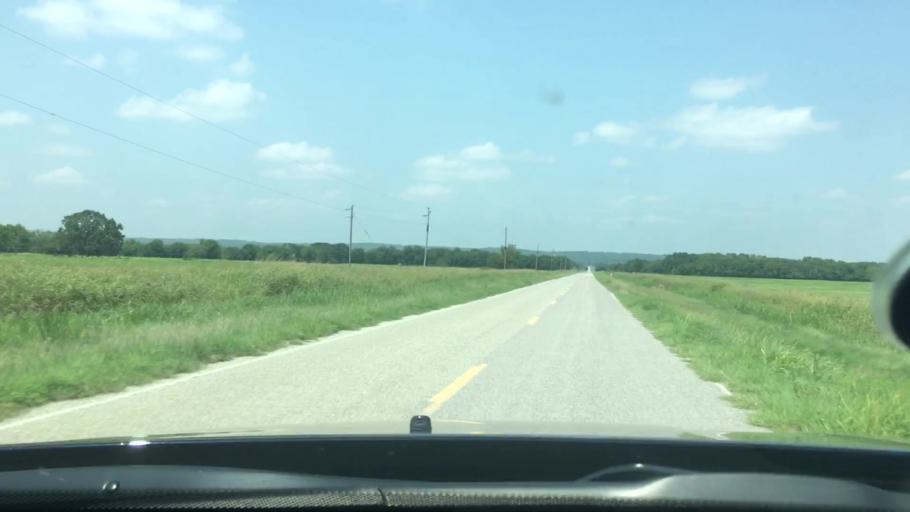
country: US
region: Oklahoma
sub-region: Johnston County
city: Tishomingo
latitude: 34.3790
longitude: -96.4962
